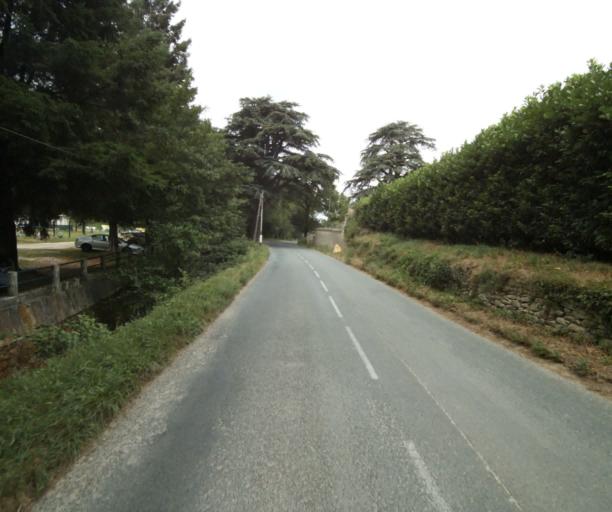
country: FR
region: Midi-Pyrenees
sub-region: Departement du Tarn
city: Soreze
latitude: 43.4470
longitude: 2.0772
